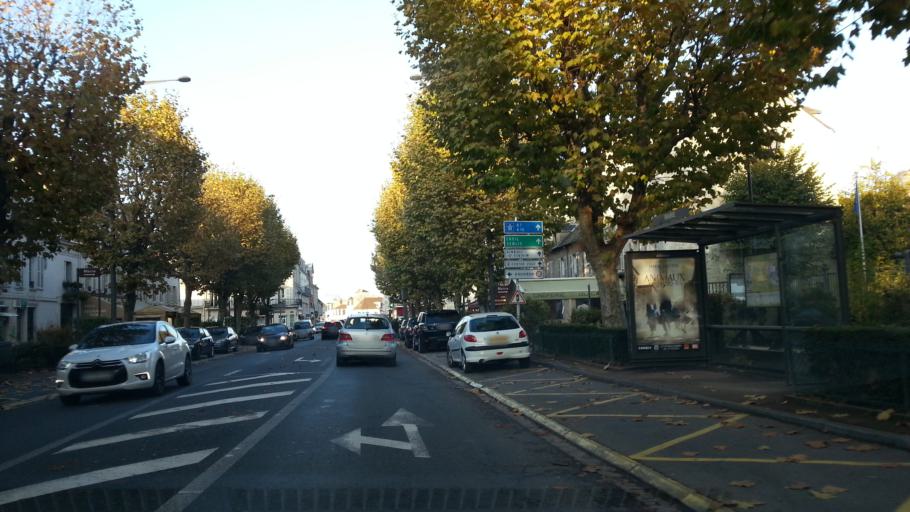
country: FR
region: Picardie
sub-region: Departement de l'Oise
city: Chantilly
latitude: 49.1924
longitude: 2.4646
